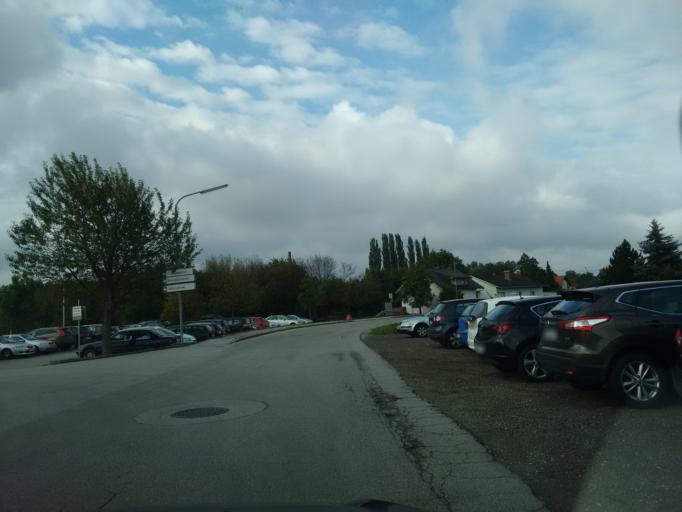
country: AT
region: Upper Austria
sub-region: Politischer Bezirk Linz-Land
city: Horsching
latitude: 48.2082
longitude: 14.2041
